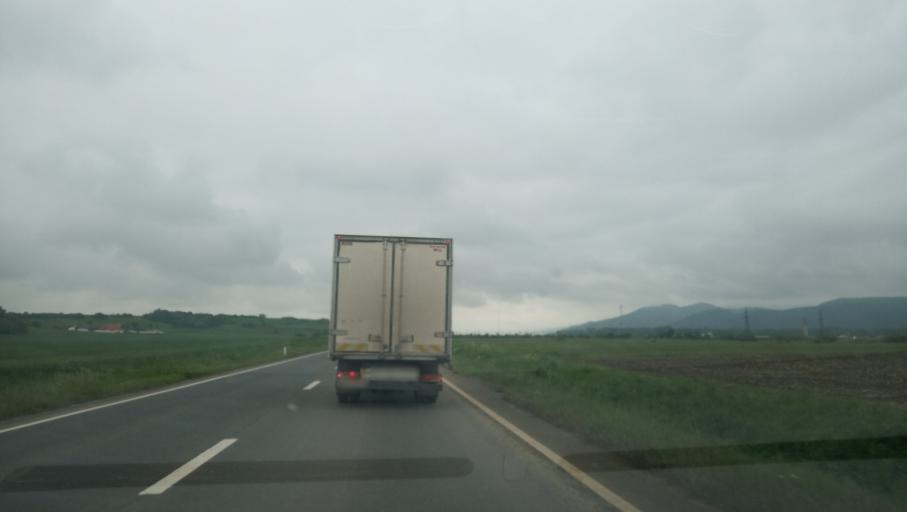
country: RO
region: Alba
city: Vurpar
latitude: 45.9709
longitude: 23.4558
